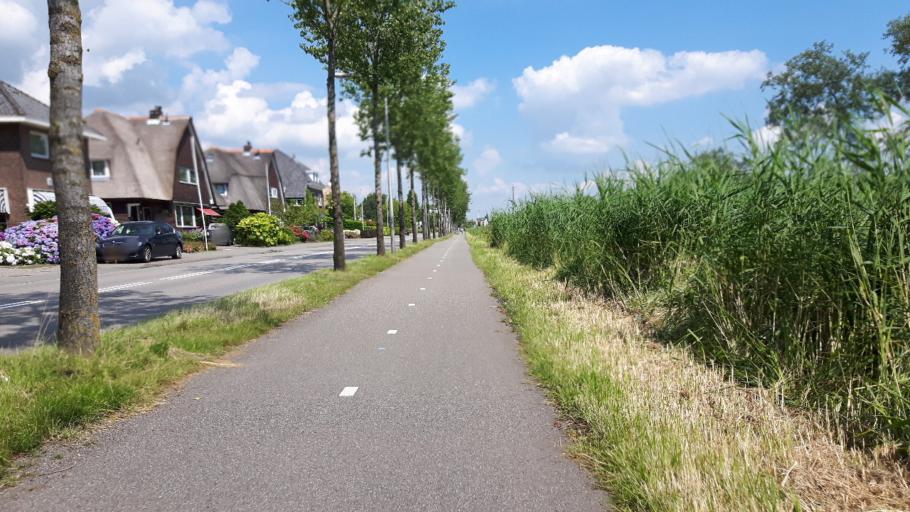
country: NL
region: South Holland
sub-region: Gemeente Gouda
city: Gouda
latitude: 52.0300
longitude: 4.7196
